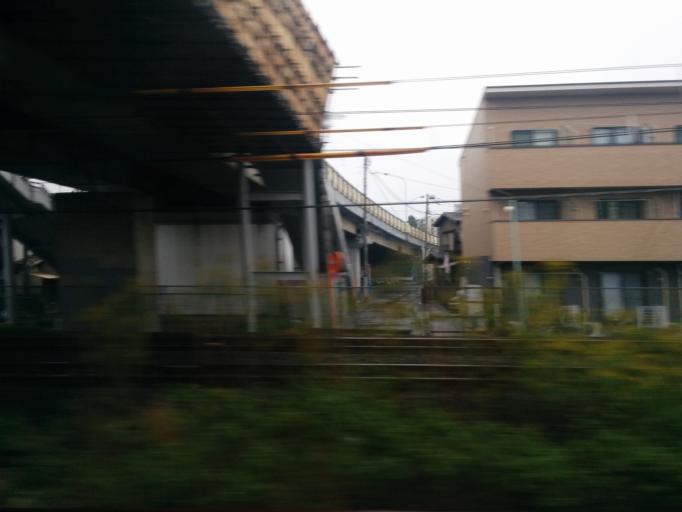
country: JP
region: Tokyo
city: Urayasu
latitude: 35.7218
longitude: 139.8656
